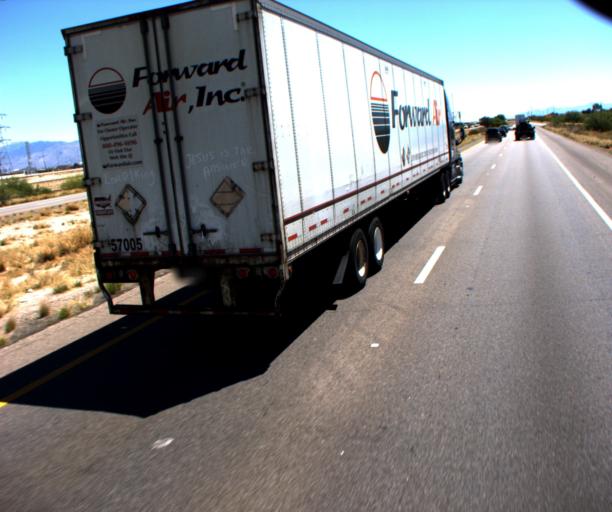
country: US
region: Arizona
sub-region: Pima County
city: Tucson
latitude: 32.1561
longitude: -110.9071
